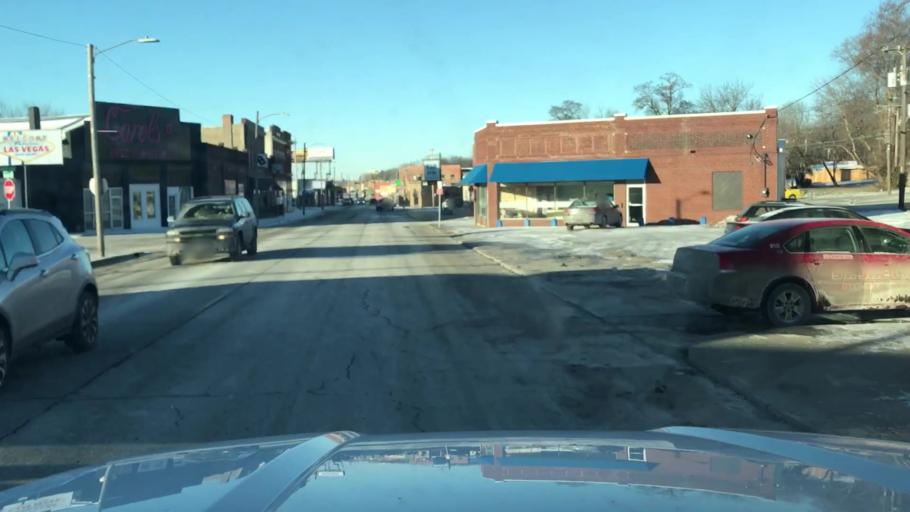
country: US
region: Missouri
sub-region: Buchanan County
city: Saint Joseph
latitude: 39.7745
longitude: -94.8361
